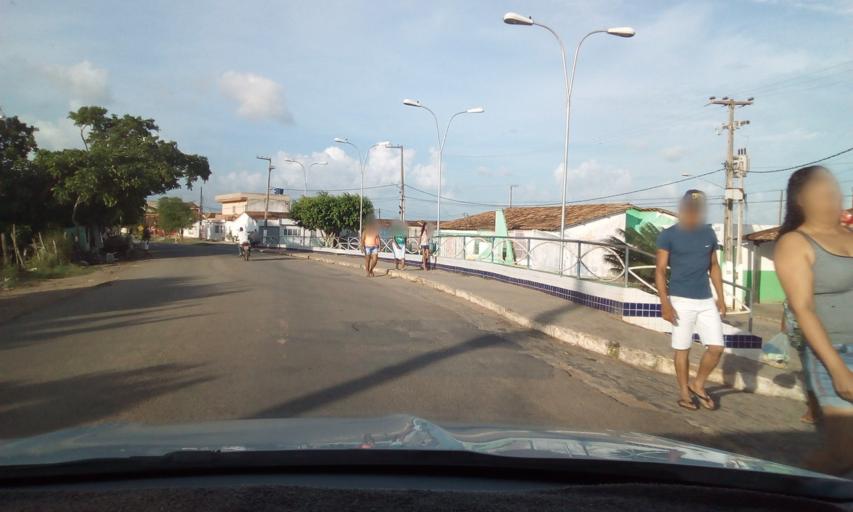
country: BR
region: Pernambuco
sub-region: Gloria Do Goita
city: Gloria do Goita
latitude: -7.9948
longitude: -35.2083
